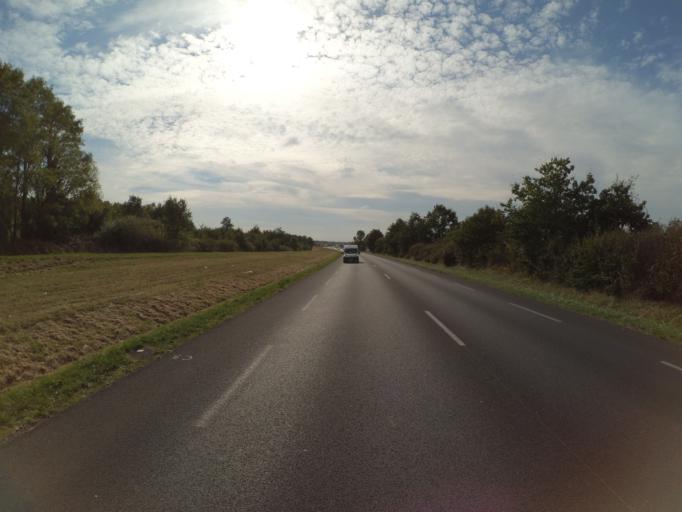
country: FR
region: Pays de la Loire
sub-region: Departement de Maine-et-Loire
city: Distre
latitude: 47.2397
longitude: -0.1115
